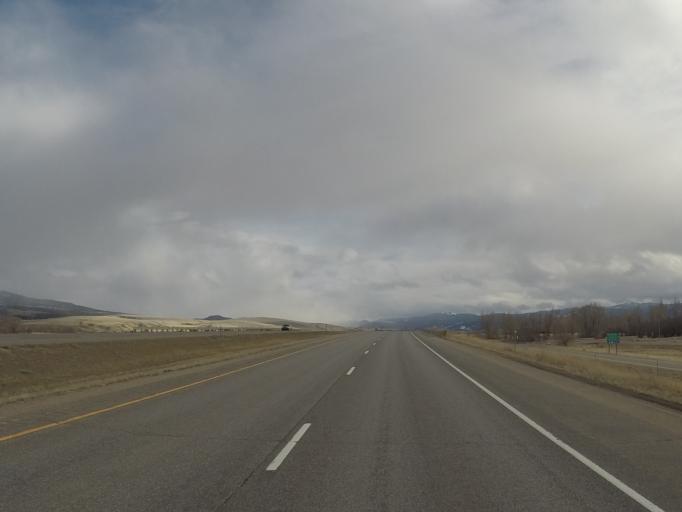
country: US
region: Montana
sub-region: Deer Lodge County
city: Warm Springs
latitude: 46.1835
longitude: -112.7836
